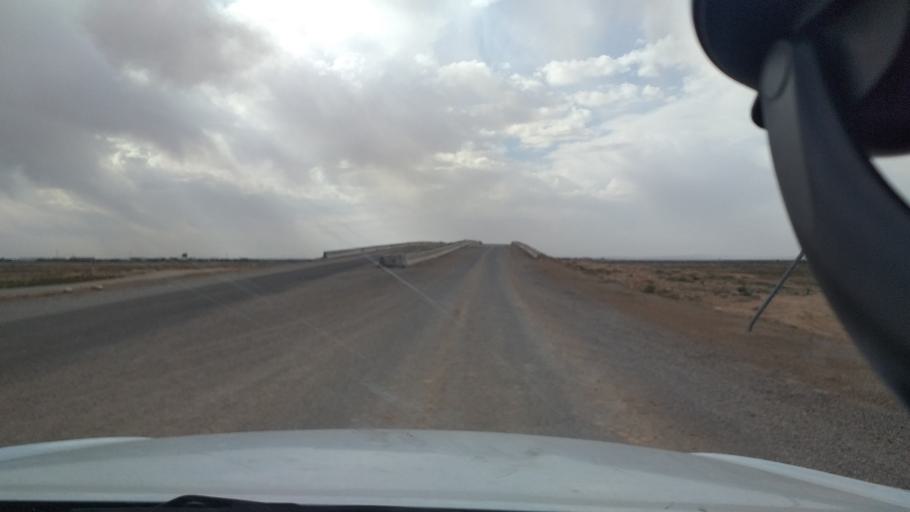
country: TN
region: Madanin
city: Medenine
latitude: 33.3021
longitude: 10.6105
